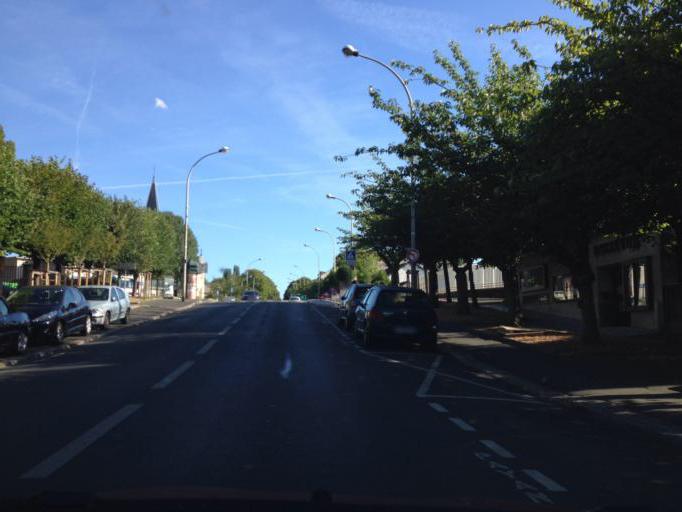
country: FR
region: Ile-de-France
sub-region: Departement des Hauts-de-Seine
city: Meudon
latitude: 48.8198
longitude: 2.2292
